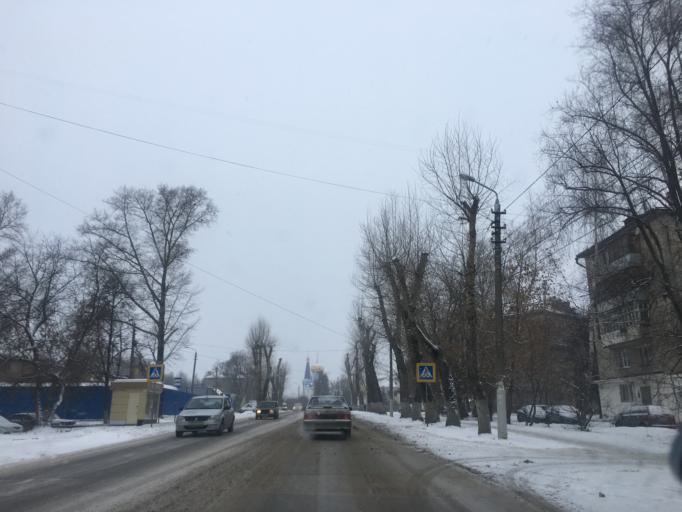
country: RU
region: Tula
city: Tula
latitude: 54.1953
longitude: 37.5620
